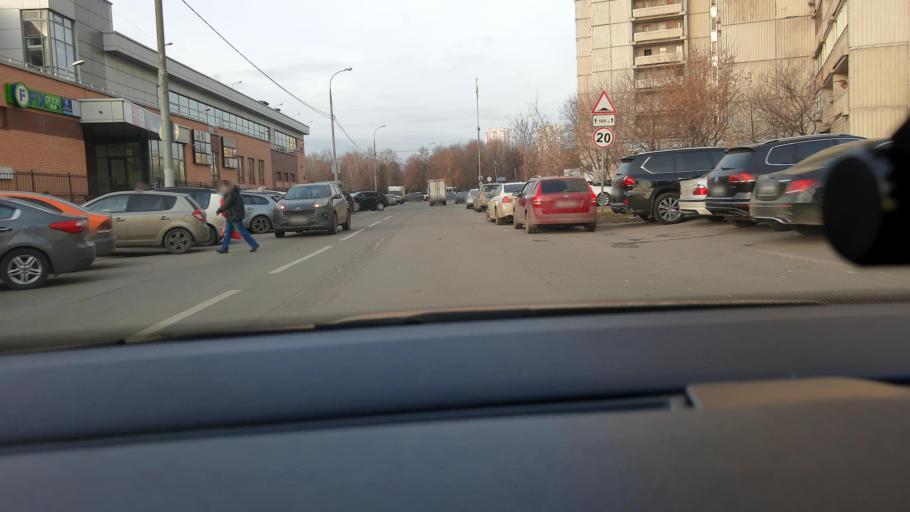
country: RU
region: Moscow
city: Mar'ino
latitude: 55.6798
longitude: 37.7165
